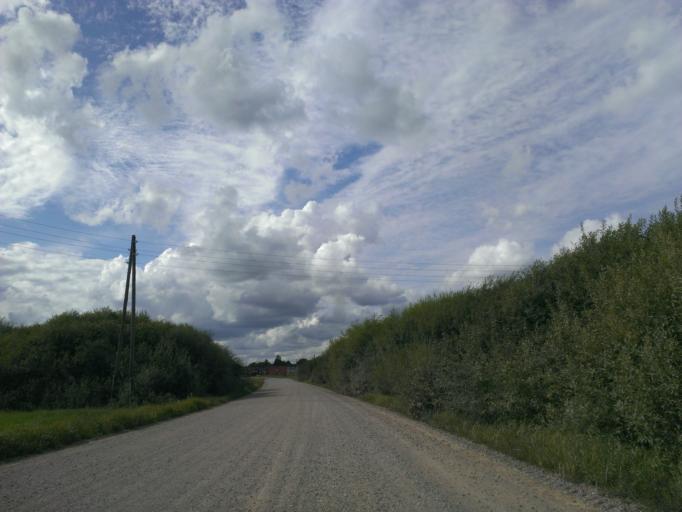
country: LV
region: Skriveri
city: Skriveri
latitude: 56.8450
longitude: 25.1714
